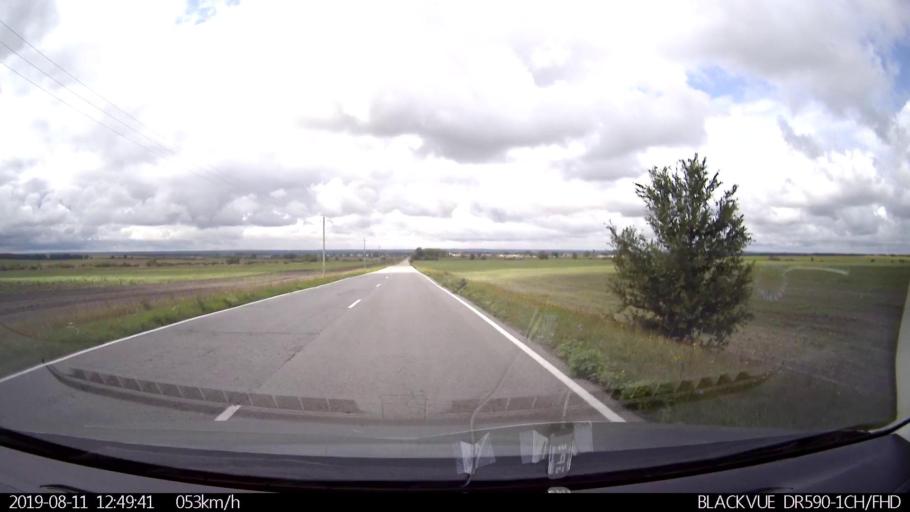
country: RU
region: Ulyanovsk
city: Ignatovka
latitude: 53.8759
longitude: 47.6829
